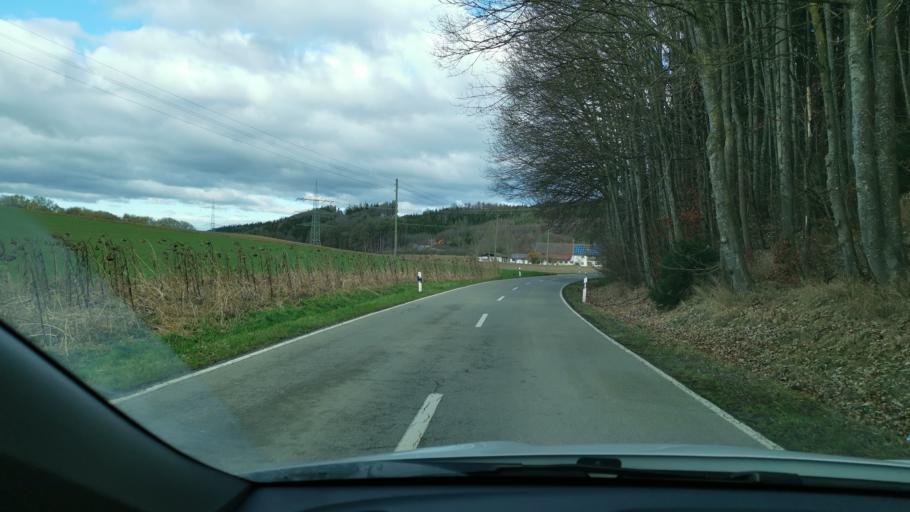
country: DE
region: Bavaria
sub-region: Swabia
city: Rehling
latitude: 48.4921
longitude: 10.9458
